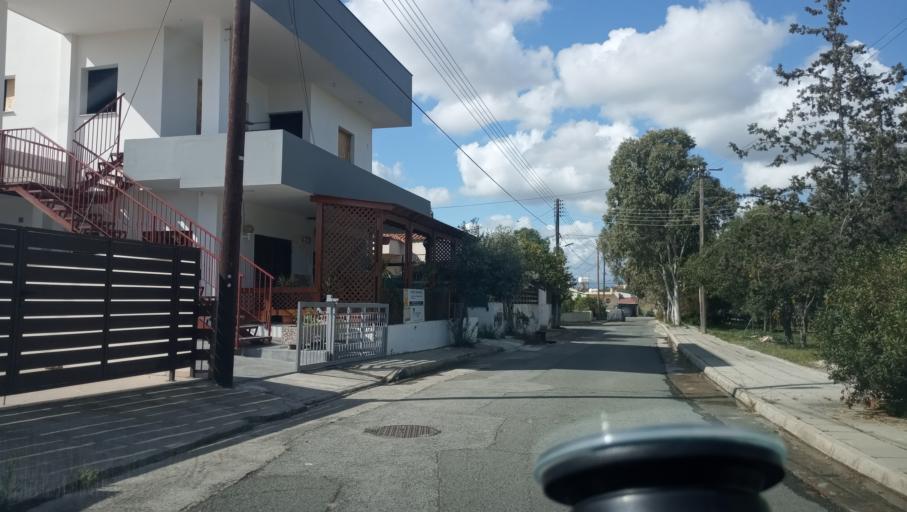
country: CY
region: Lefkosia
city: Geri
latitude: 35.1014
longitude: 33.4080
